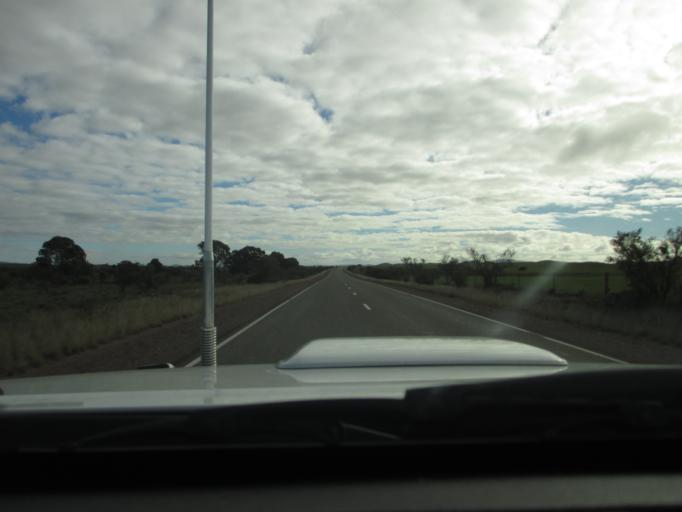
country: AU
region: South Australia
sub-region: Flinders Ranges
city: Quorn
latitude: -32.4556
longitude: 138.5373
